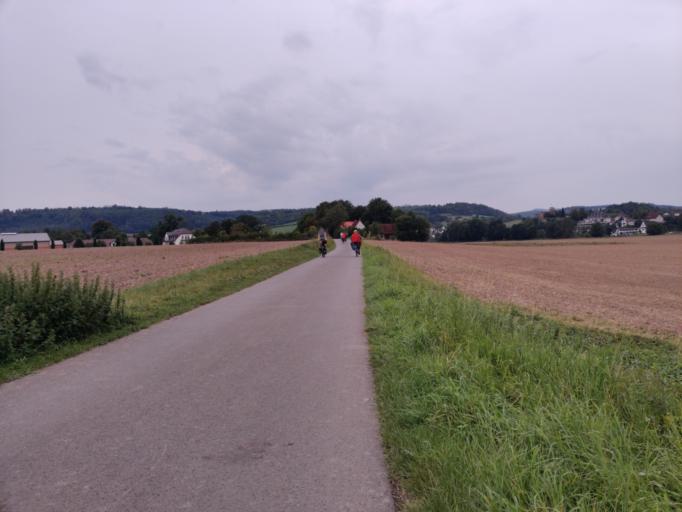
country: DE
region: Lower Saxony
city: Polle
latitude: 51.9012
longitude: 9.4175
